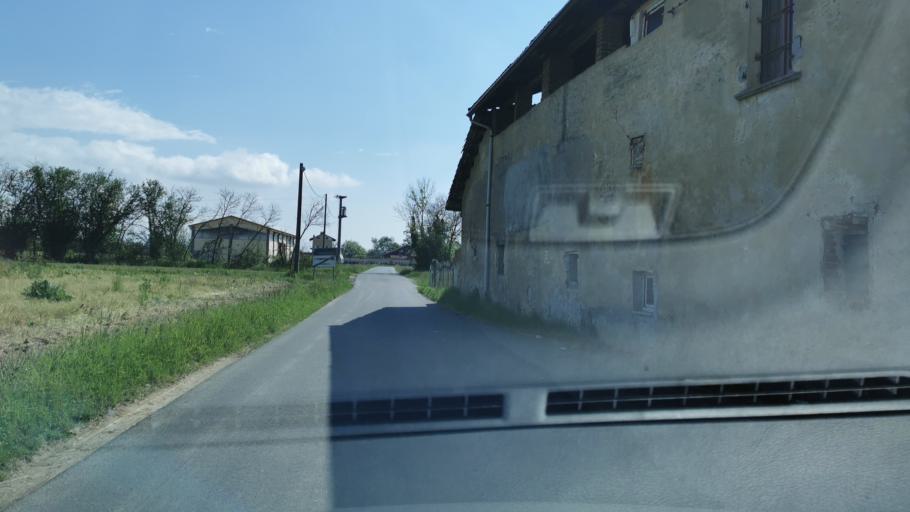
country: IT
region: Piedmont
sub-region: Provincia di Torino
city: Front
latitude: 45.2886
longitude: 7.7025
